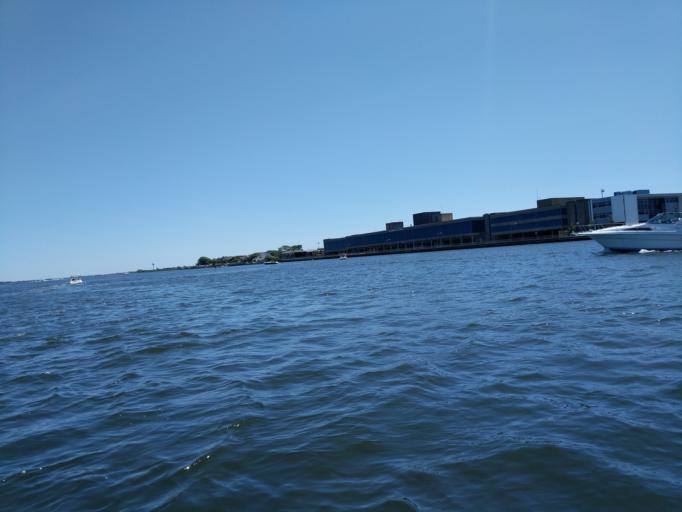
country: US
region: New York
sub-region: Nassau County
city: Barnum Island
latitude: 40.5964
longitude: -73.6374
